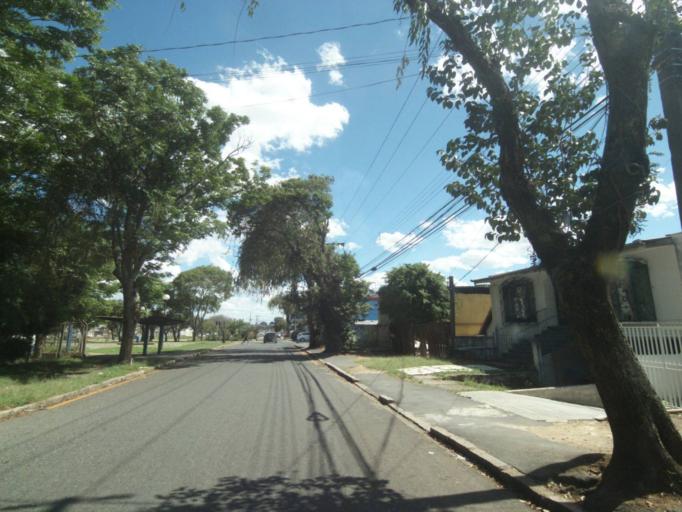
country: BR
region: Parana
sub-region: Curitiba
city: Curitiba
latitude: -25.5051
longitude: -49.3214
